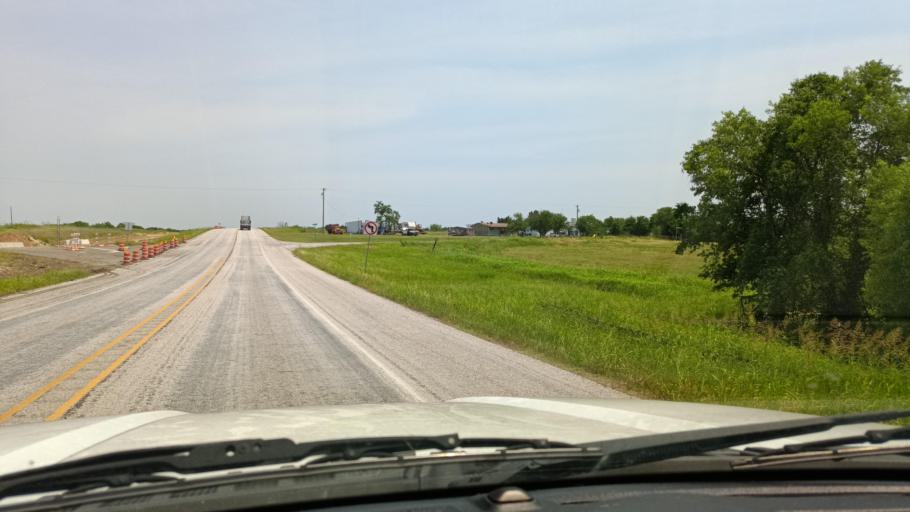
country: US
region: Texas
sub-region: Bell County
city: Rogers
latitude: 30.9668
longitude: -97.2652
